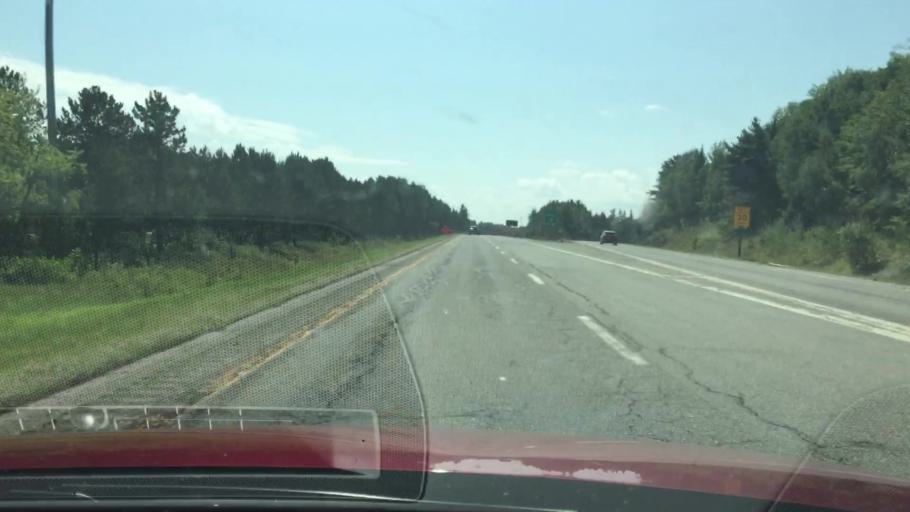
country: US
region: Maine
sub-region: Penobscot County
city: Patten
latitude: 45.8765
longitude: -68.4116
